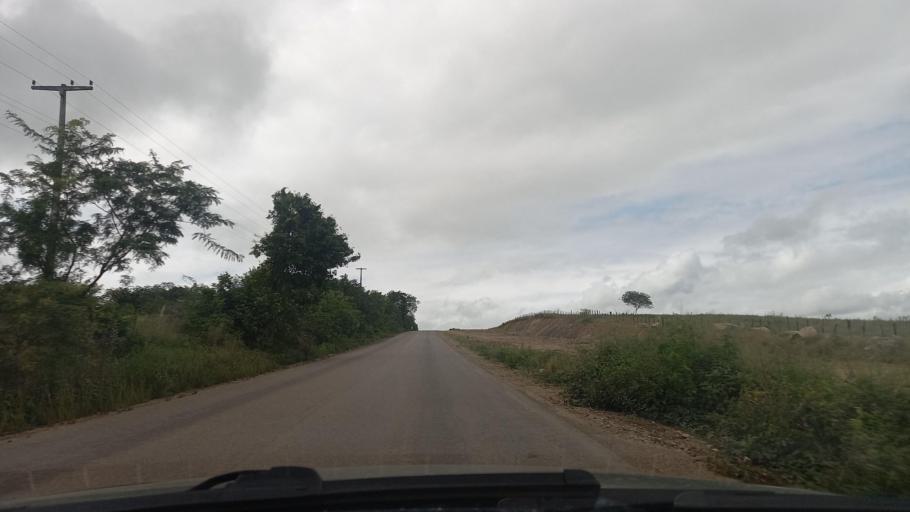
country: BR
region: Alagoas
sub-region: Batalha
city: Batalha
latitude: -9.6433
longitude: -37.1919
